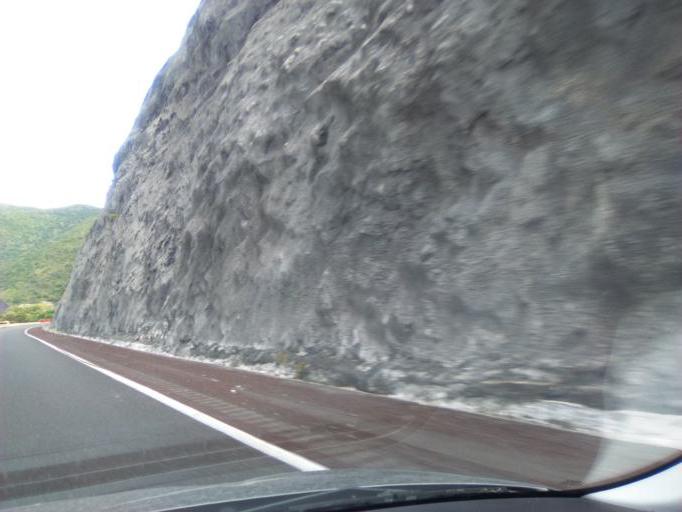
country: MX
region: Guerrero
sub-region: Eduardo Neri
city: Tlanipatla
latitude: 17.8539
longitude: -99.4167
